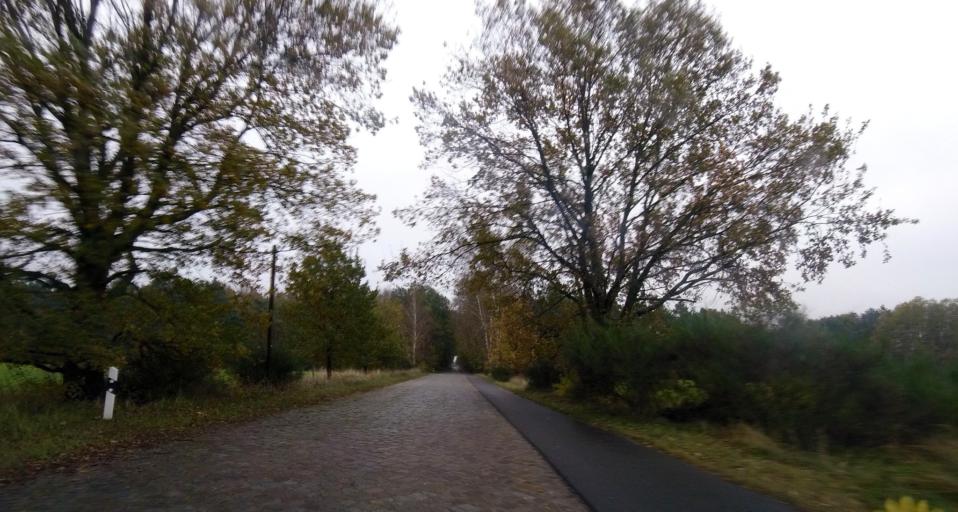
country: DE
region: Brandenburg
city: Niedergorsdorf
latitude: 51.9999
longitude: 12.9698
